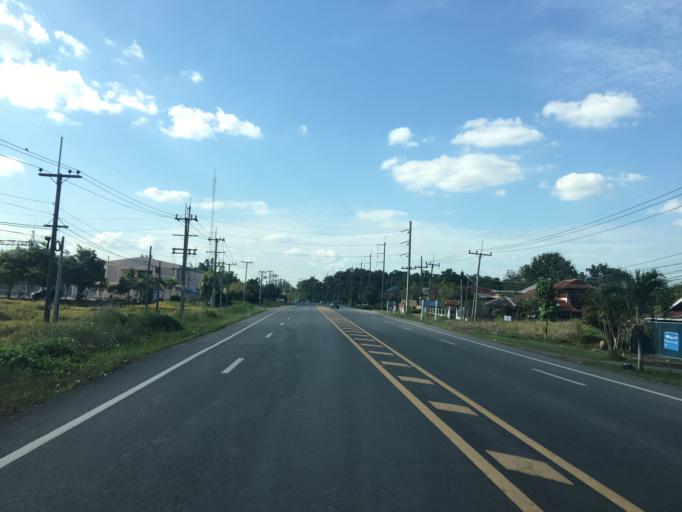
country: TH
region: Phayao
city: Chun
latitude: 19.3322
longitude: 100.1391
